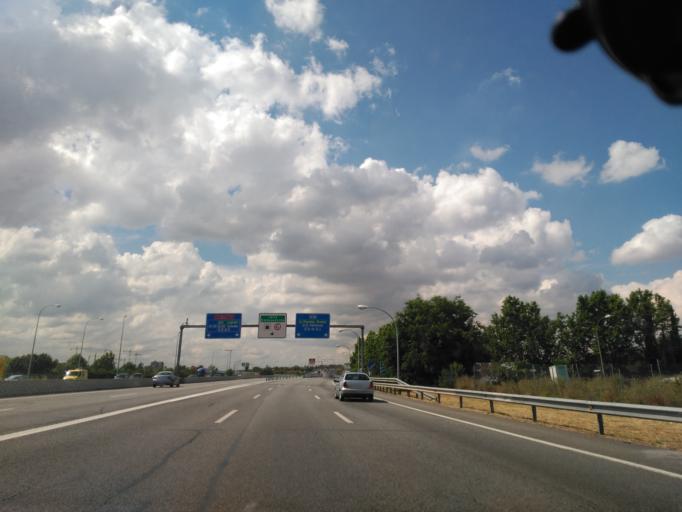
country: ES
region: Madrid
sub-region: Provincia de Madrid
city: Usera
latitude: 40.3768
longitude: -3.6843
